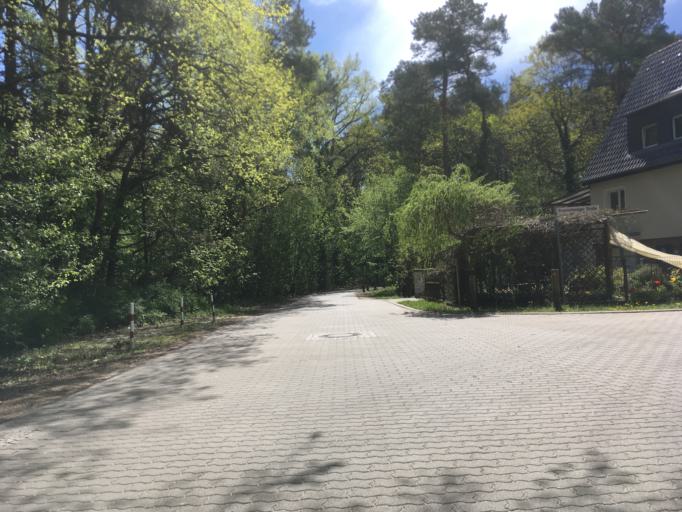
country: DE
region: Brandenburg
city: Zeuthen
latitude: 52.3541
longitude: 13.6019
